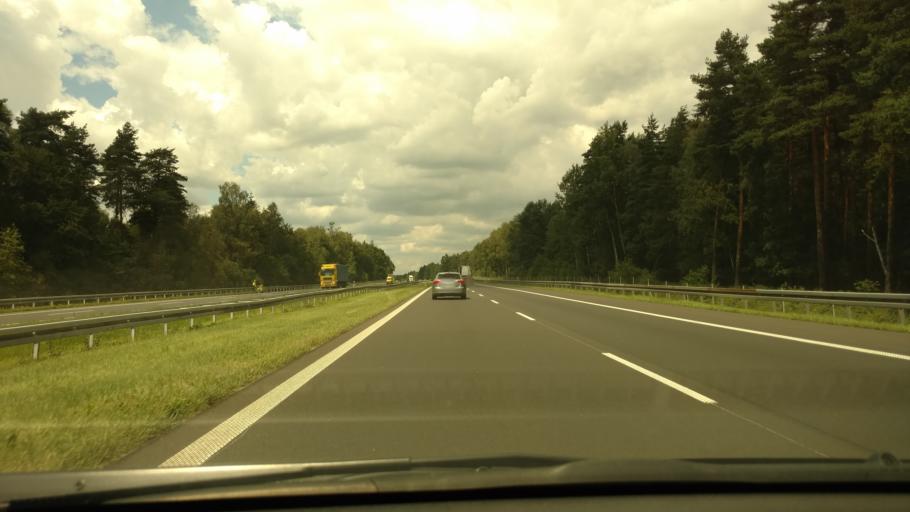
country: PL
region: Lesser Poland Voivodeship
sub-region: Powiat chrzanowski
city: Bolecin
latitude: 50.1300
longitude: 19.4806
